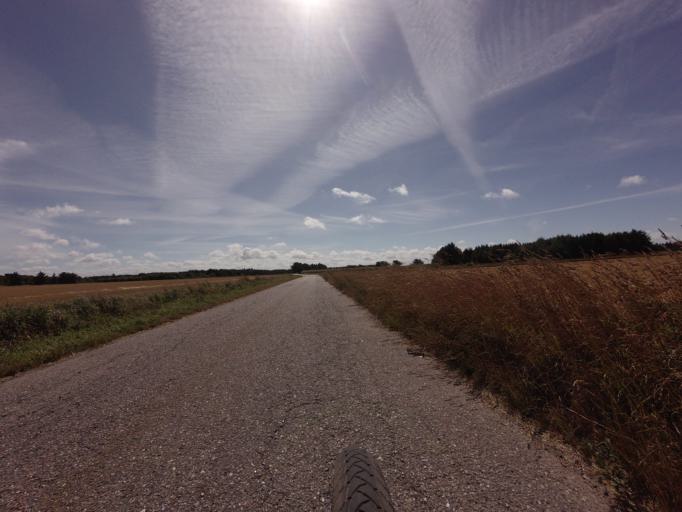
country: DK
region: North Denmark
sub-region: Hjorring Kommune
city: Vra
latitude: 57.3825
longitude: 9.7836
